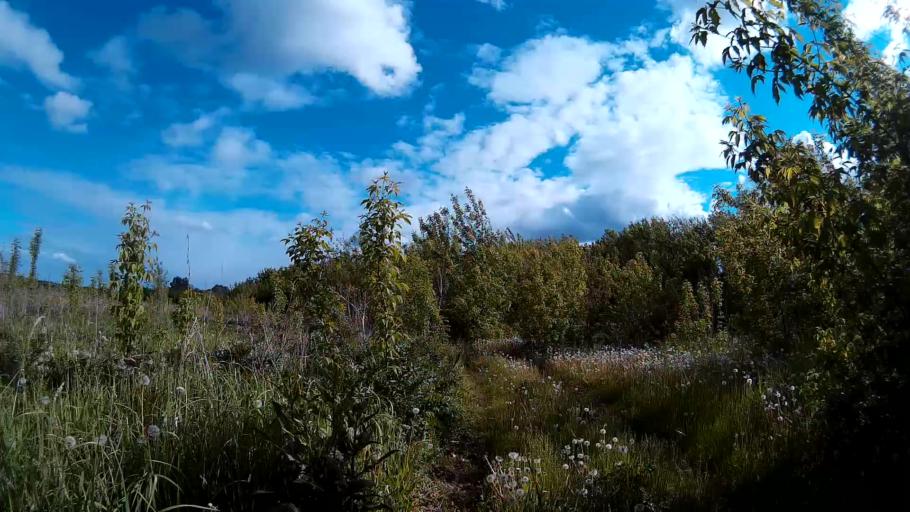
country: RU
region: Ulyanovsk
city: Novoul'yanovsk
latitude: 54.2183
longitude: 48.2569
